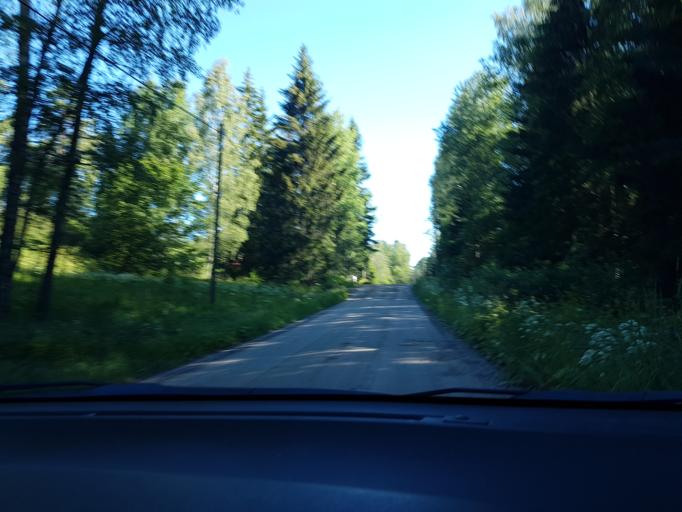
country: FI
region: Uusimaa
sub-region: Helsinki
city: Sibbo
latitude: 60.2792
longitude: 25.2367
